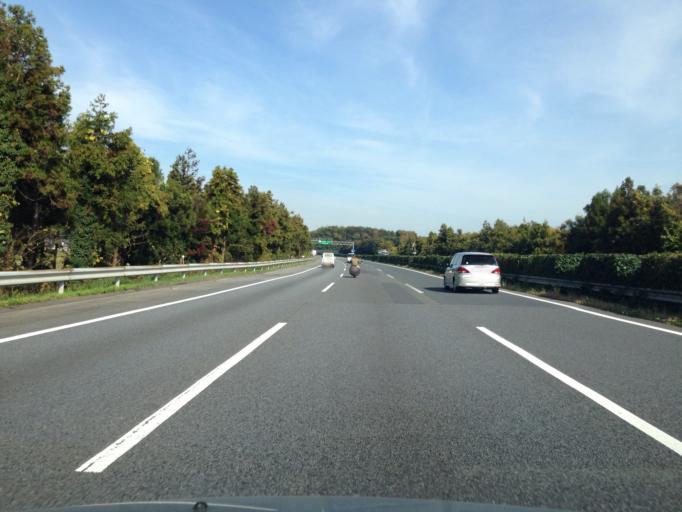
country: JP
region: Ibaraki
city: Naka
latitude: 36.0998
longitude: 140.1721
